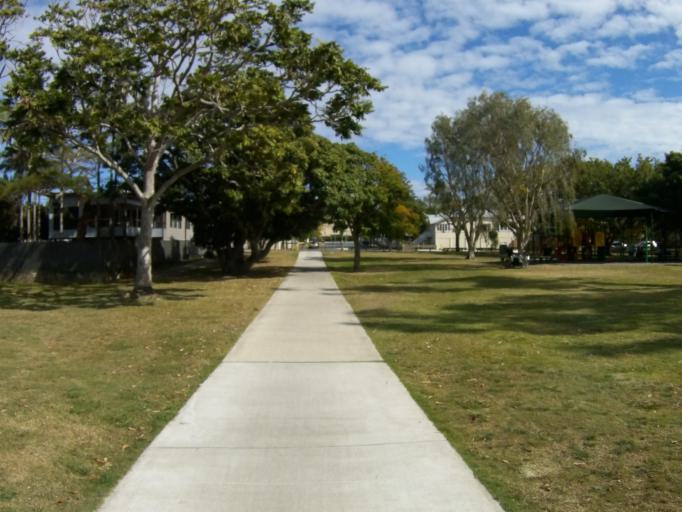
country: AU
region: Queensland
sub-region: Brisbane
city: Greenslopes
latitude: -27.4990
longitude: 153.0426
